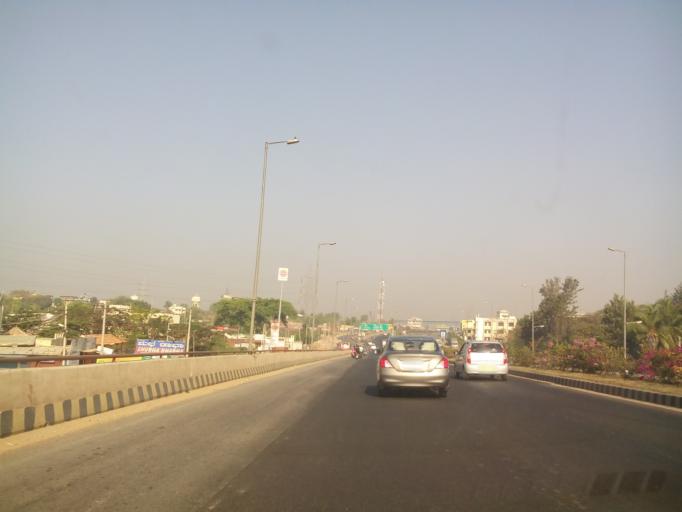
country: IN
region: Karnataka
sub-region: Bangalore Rural
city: Nelamangala
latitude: 13.0930
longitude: 77.3936
